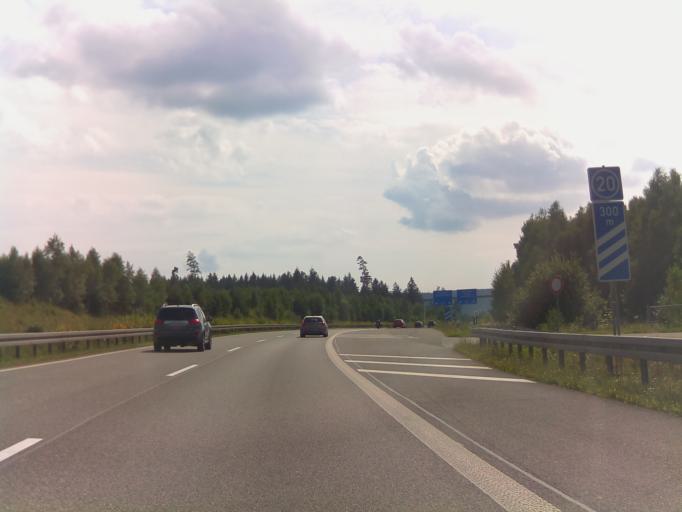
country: DE
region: Thuringia
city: Suhl
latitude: 50.6142
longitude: 10.6562
